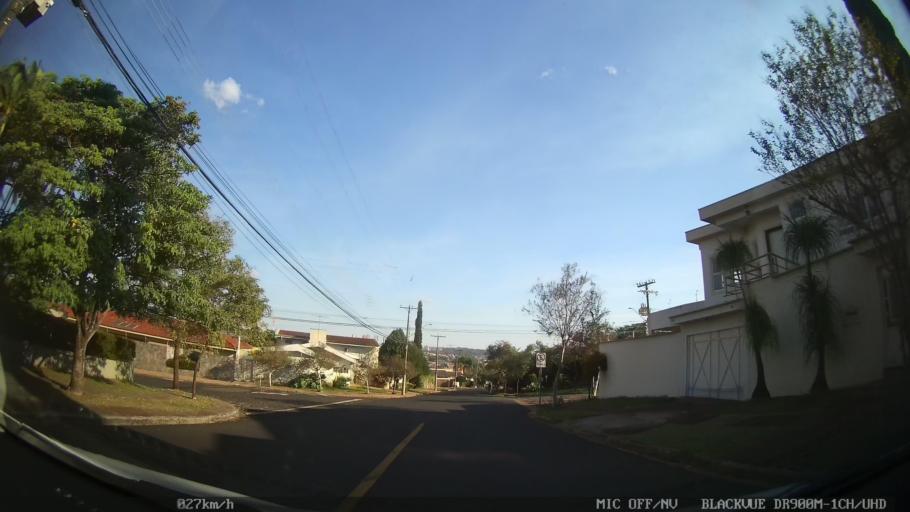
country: BR
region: Sao Paulo
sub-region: Ribeirao Preto
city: Ribeirao Preto
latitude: -21.2041
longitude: -47.7782
